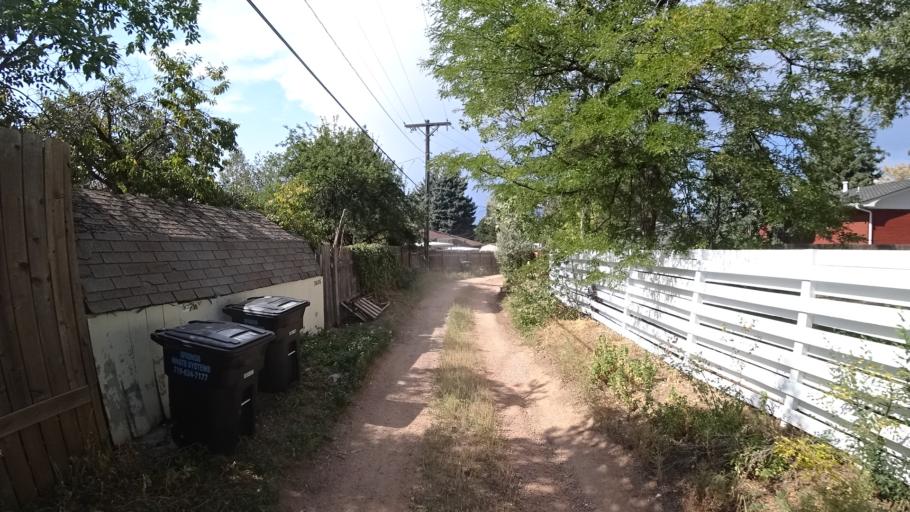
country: US
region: Colorado
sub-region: El Paso County
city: Colorado Springs
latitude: 38.8665
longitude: -104.7708
